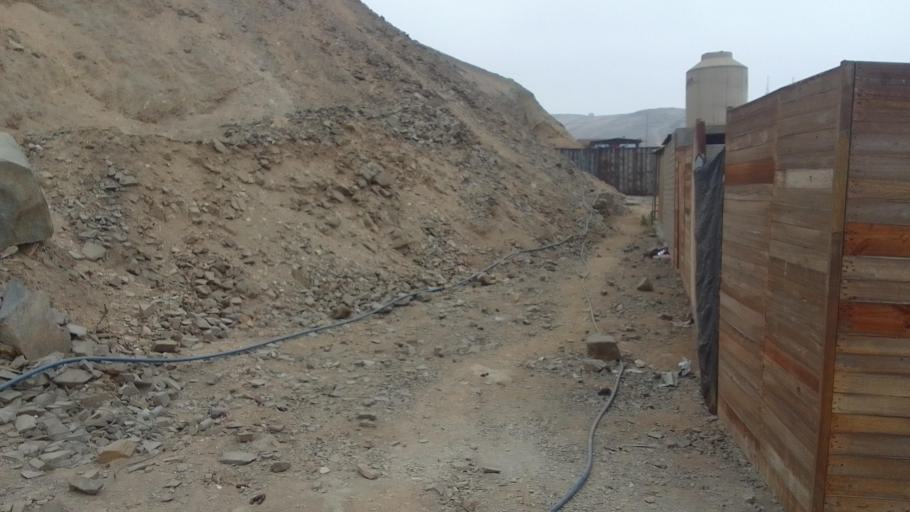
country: PE
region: Lima
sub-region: Lima
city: Santa Rosa
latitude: -11.8152
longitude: -77.1224
